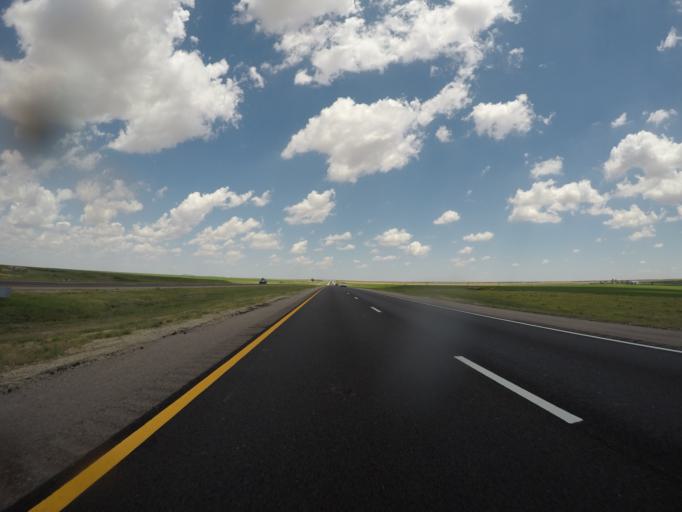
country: US
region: Kansas
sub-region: Sherman County
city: Goodland
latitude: 39.3300
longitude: -101.4835
